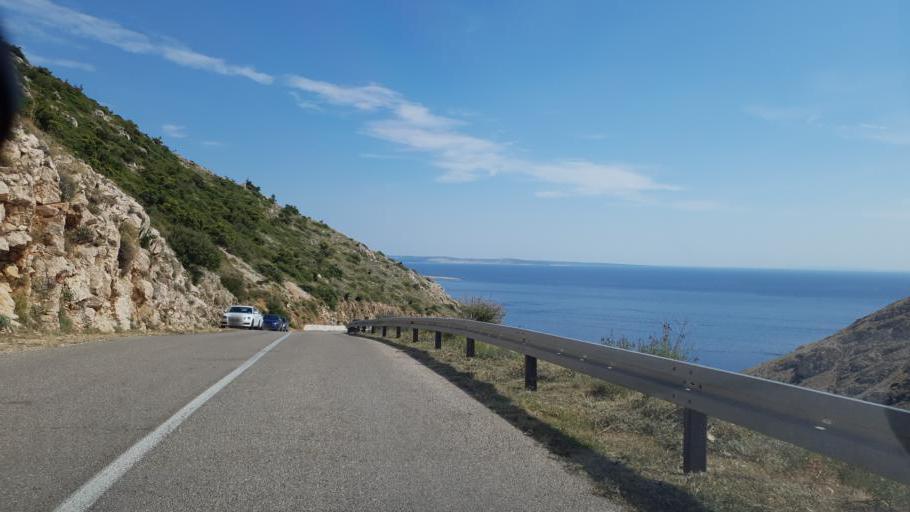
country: HR
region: Primorsko-Goranska
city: Punat
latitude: 44.9716
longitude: 14.6623
